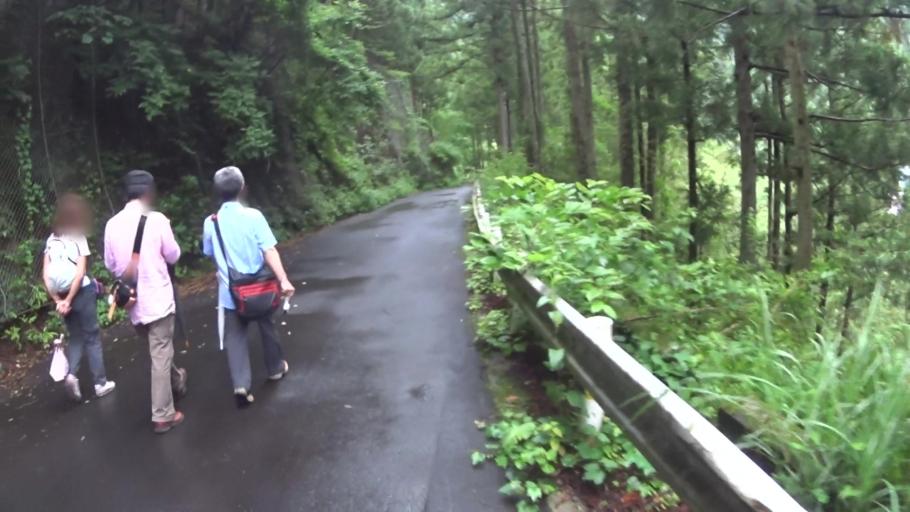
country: JP
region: Tokyo
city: Itsukaichi
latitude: 35.8011
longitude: 139.0818
